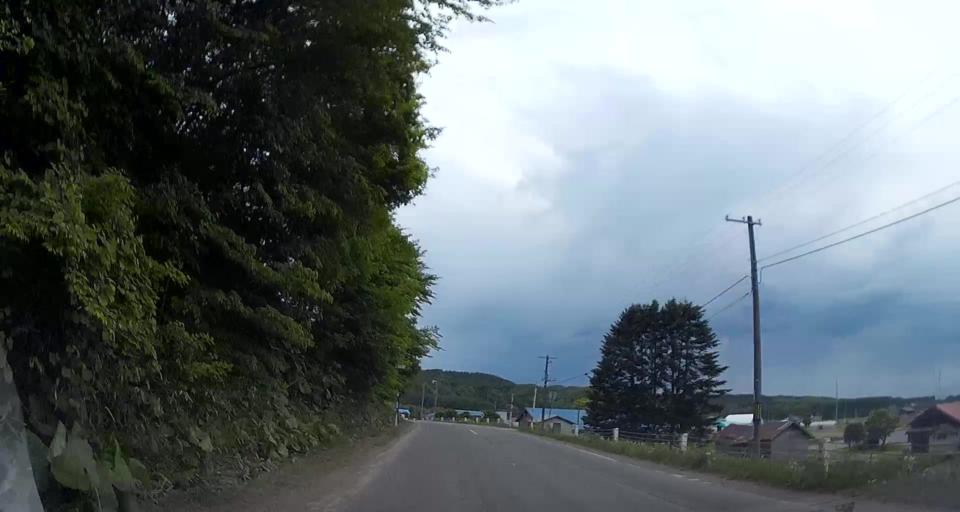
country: JP
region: Hokkaido
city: Chitose
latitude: 42.7570
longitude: 141.9785
